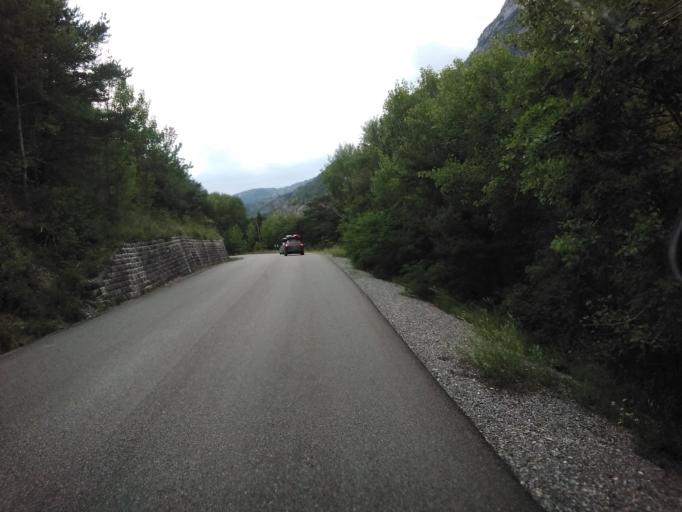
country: FR
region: Provence-Alpes-Cote d'Azur
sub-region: Departement des Alpes-de-Haute-Provence
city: Seyne-les-Alpes
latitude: 44.4472
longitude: 6.4061
